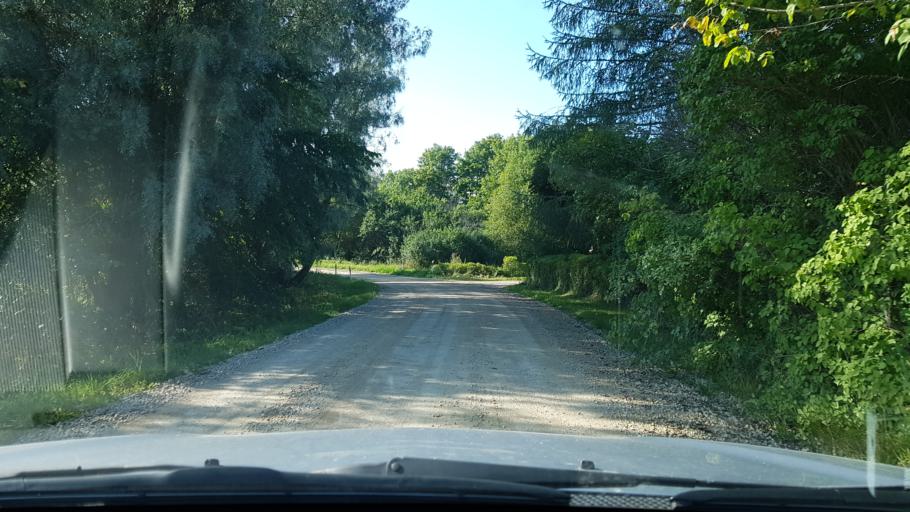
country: EE
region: Ida-Virumaa
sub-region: Narva-Joesuu linn
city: Narva-Joesuu
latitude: 59.4093
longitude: 28.0160
